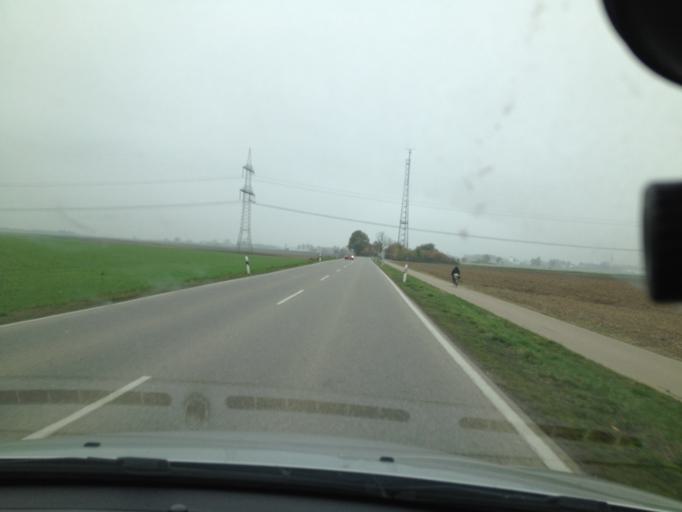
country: DE
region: Bavaria
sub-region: Swabia
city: Untermeitingen
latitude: 48.1665
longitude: 10.7870
